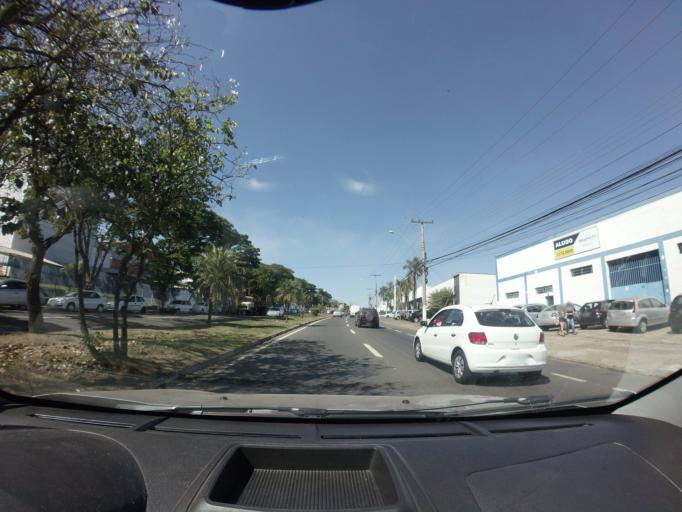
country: BR
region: Sao Paulo
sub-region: Piracicaba
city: Piracicaba
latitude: -22.7297
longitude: -47.6152
